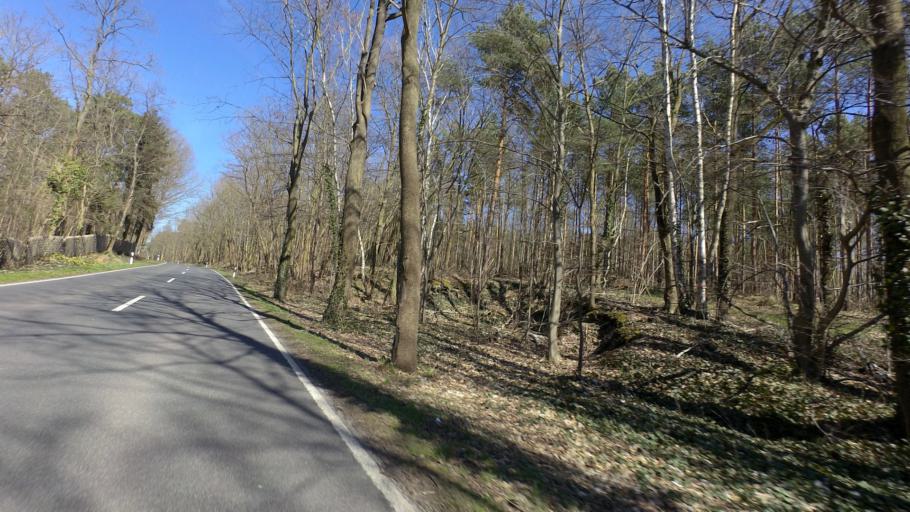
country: DE
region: Brandenburg
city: Diensdorf-Radlow
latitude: 52.2512
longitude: 14.0721
